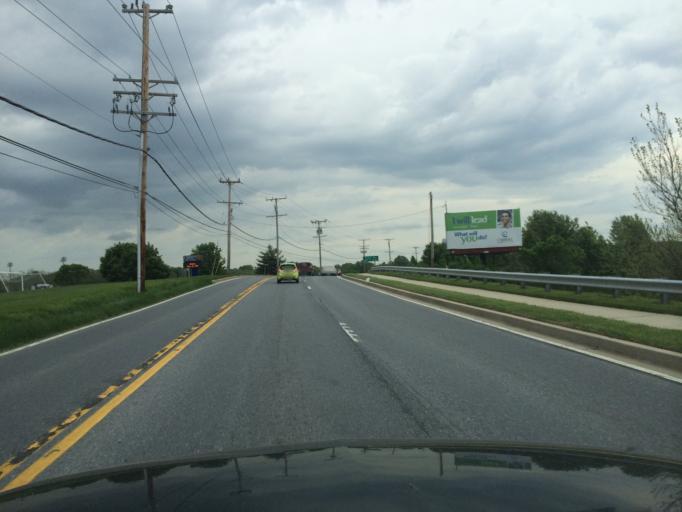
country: US
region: Maryland
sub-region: Carroll County
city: Eldersburg
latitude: 39.4112
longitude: -76.9498
